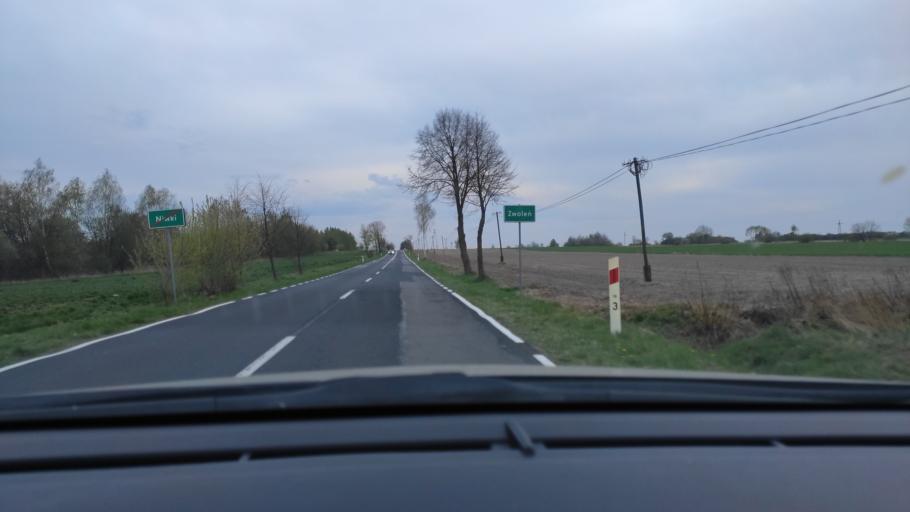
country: PL
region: Masovian Voivodeship
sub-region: Powiat zwolenski
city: Zwolen
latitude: 51.3750
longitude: 21.5630
